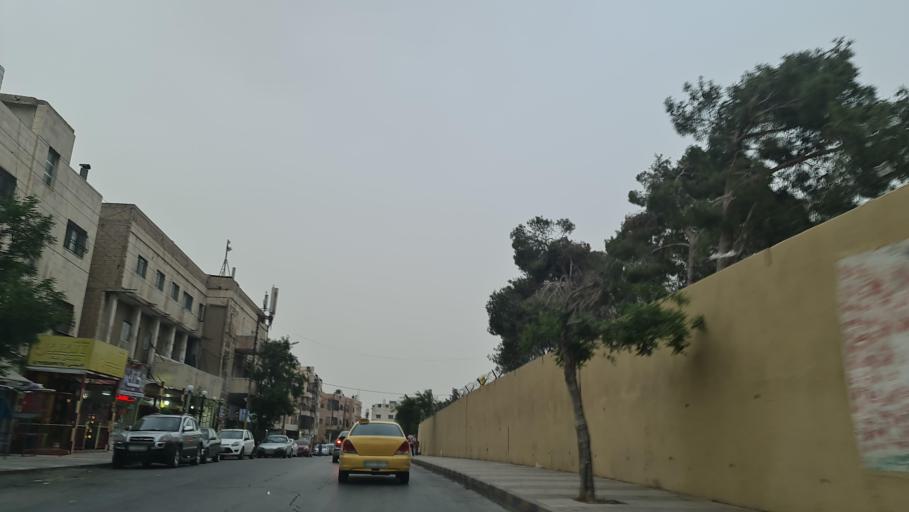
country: JO
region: Amman
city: Amman
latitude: 31.9421
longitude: 35.9388
